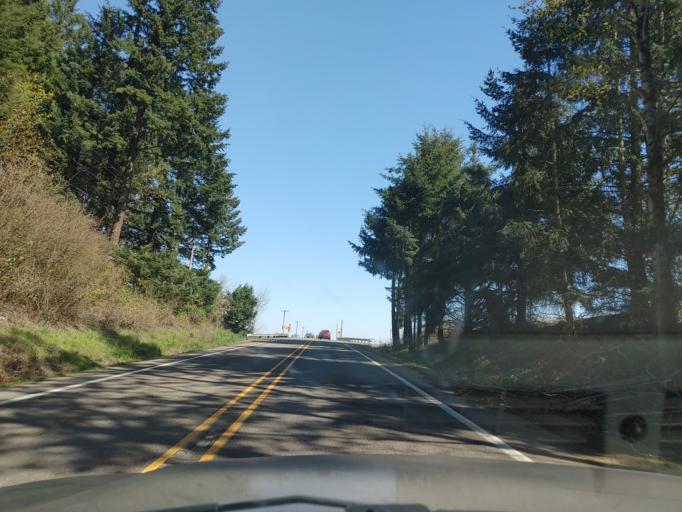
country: US
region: Oregon
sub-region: Marion County
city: Hubbard
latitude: 45.2290
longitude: -122.8823
